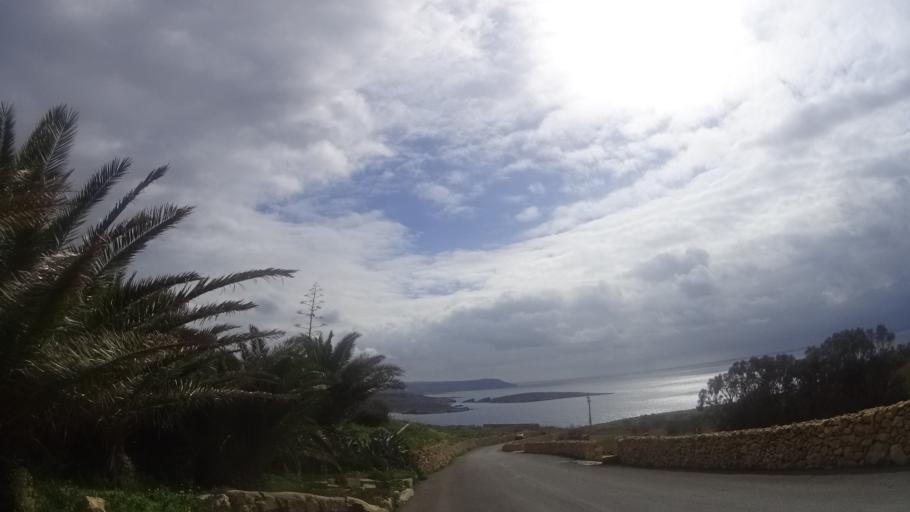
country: MT
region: Il-Qala
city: Qala
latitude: 36.0324
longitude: 14.3215
